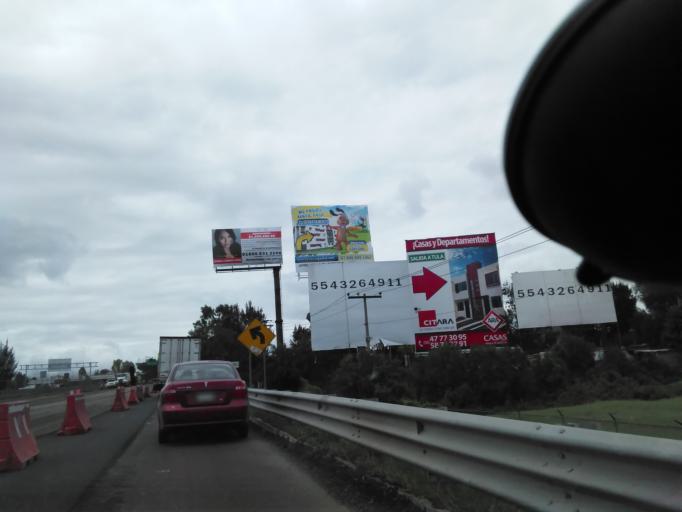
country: MX
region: Mexico
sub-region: Huehuetoca
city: Jorobas
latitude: 19.8236
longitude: -99.2465
